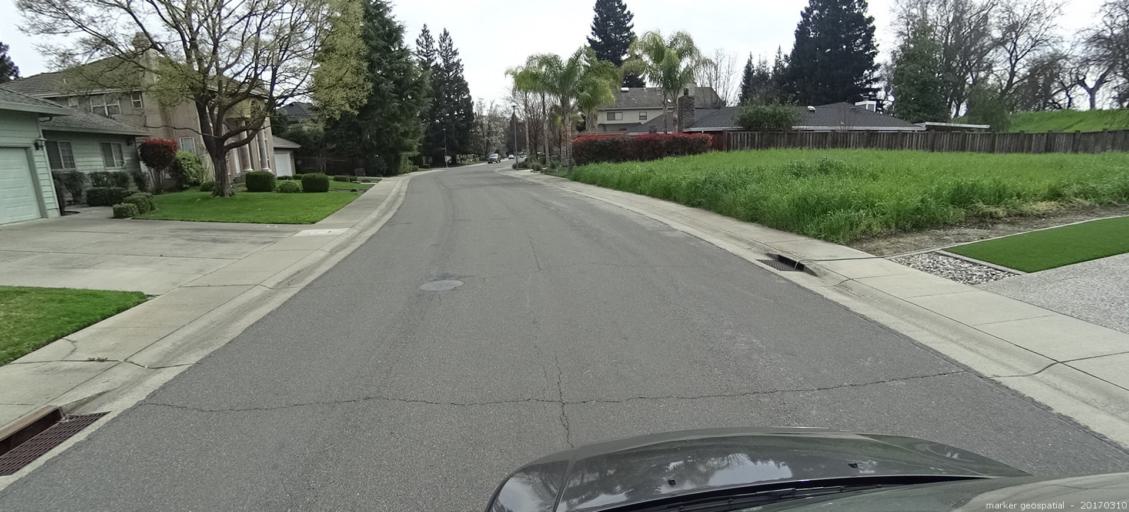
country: US
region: California
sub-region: Sacramento County
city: Parkway
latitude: 38.4774
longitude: -121.5406
